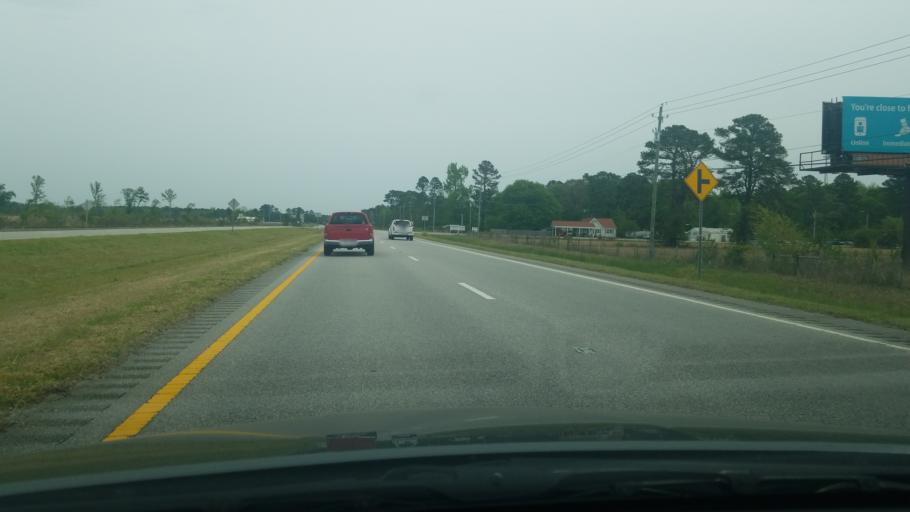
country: US
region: North Carolina
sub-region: Beaufort County
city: Washington
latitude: 35.4478
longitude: -77.1237
